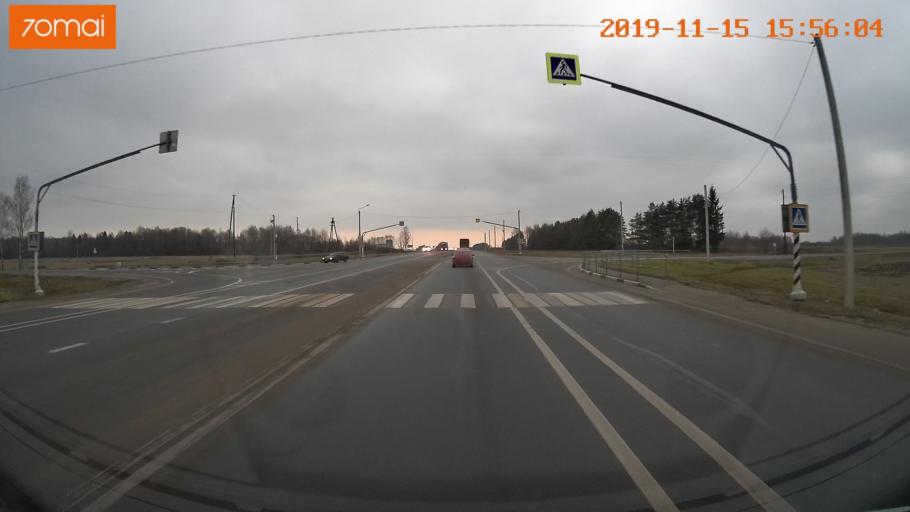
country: RU
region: Jaroslavl
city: Yaroslavl
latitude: 57.8461
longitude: 39.9772
